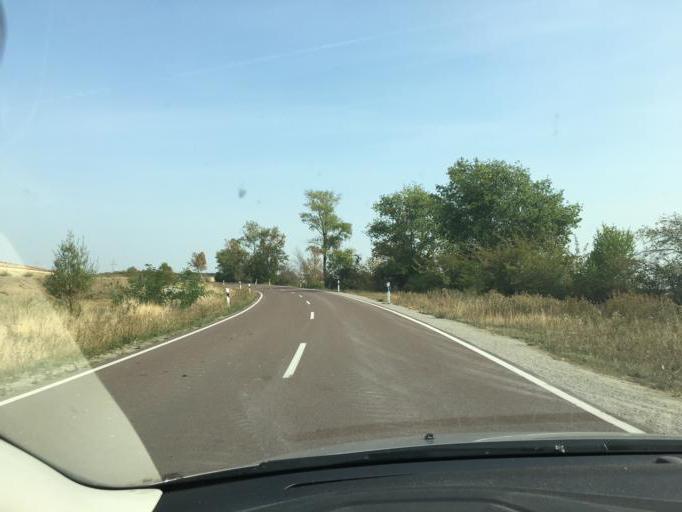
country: DE
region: Saxony-Anhalt
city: Baalberge
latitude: 51.8087
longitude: 11.8140
